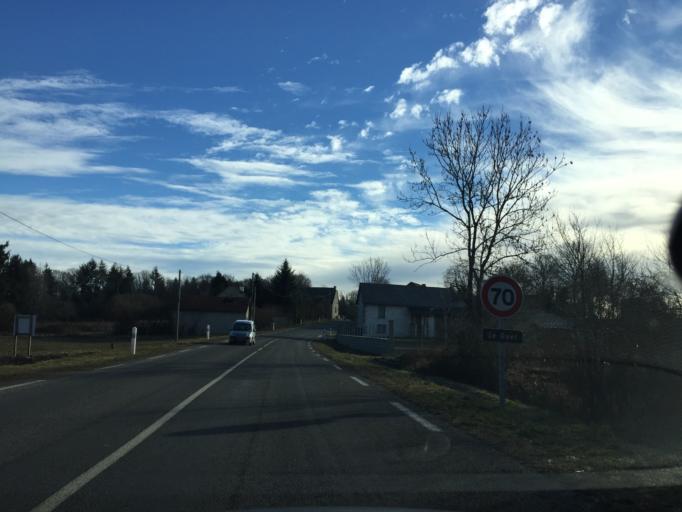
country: FR
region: Limousin
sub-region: Departement de la Creuse
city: Auzances
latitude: 45.8766
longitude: 2.5081
